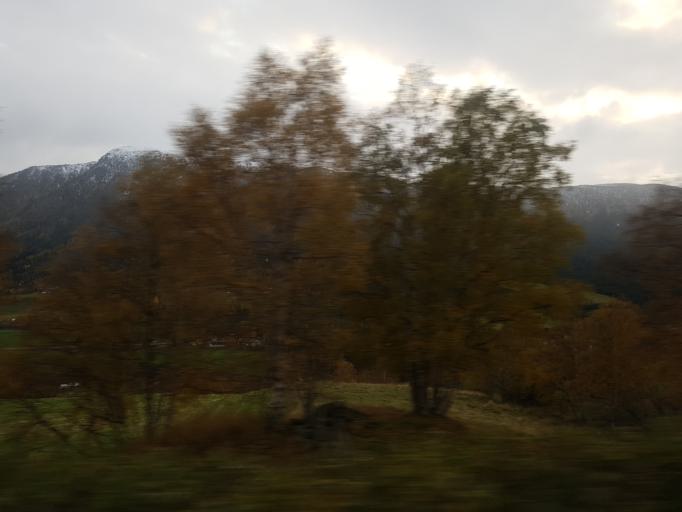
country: NO
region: Oppland
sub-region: Dovre
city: Dombas
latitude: 62.0282
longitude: 9.1786
